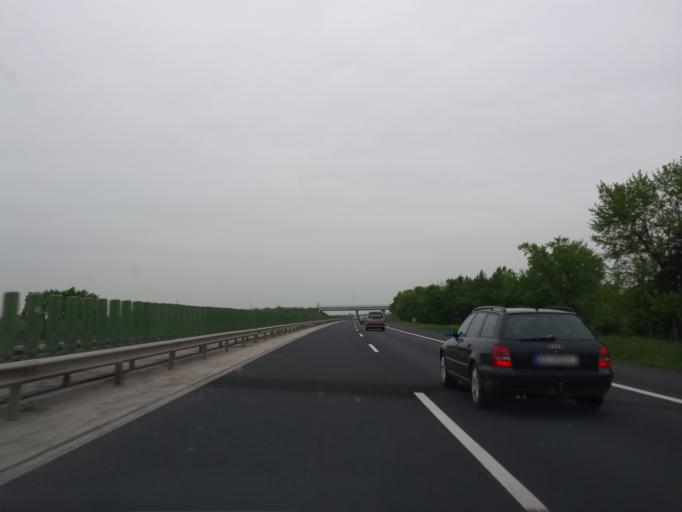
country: AT
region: Burgenland
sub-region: Politischer Bezirk Neusiedl am See
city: Nickelsdorf
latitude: 47.9055
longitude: 17.1473
